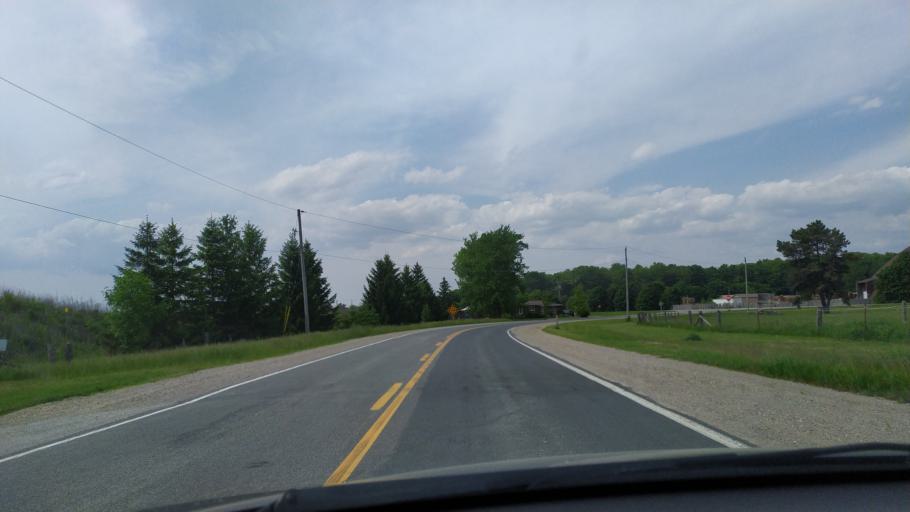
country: CA
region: Ontario
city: Ingersoll
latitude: 43.0471
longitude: -80.9816
